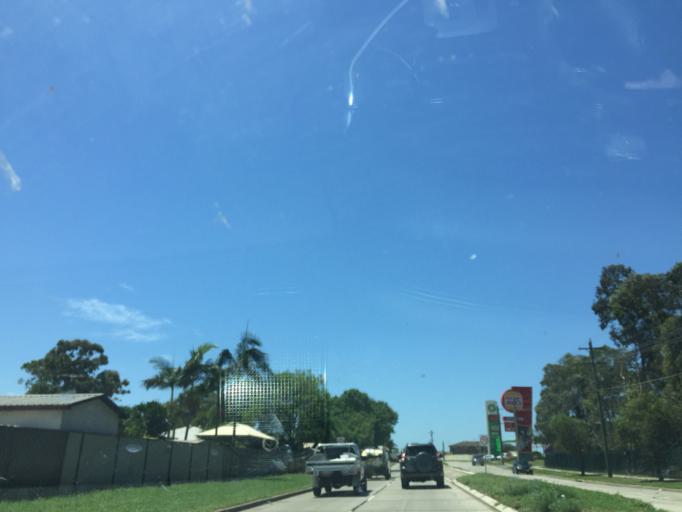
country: AU
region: New South Wales
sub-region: Blacktown
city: Glendenning
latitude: -33.7360
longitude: 150.8522
